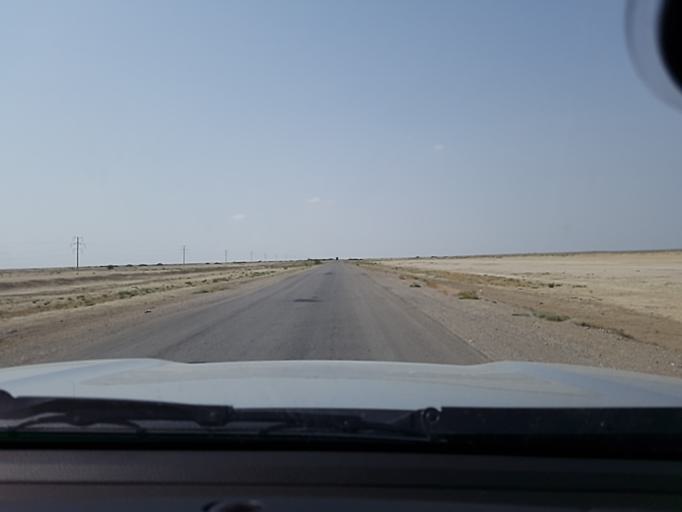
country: TM
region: Balkan
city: Gumdag
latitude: 38.9421
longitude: 54.5898
